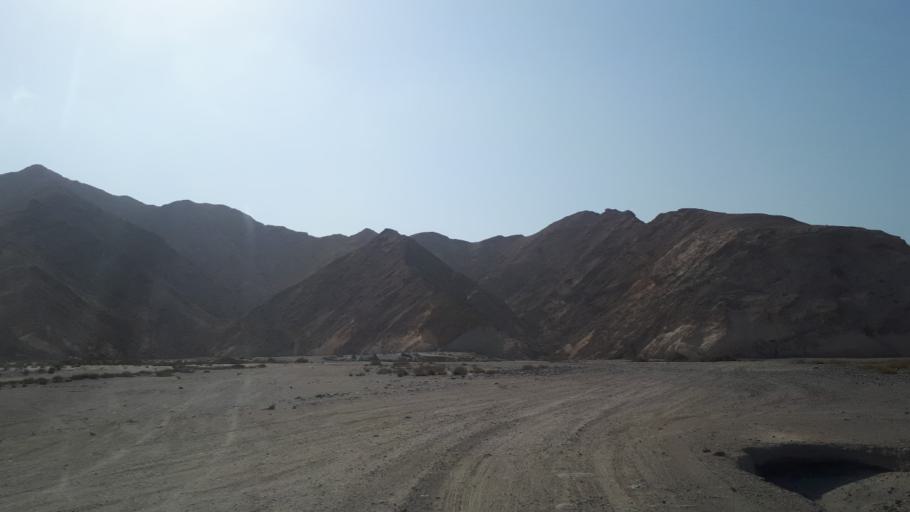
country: OM
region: Muhafazat Masqat
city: Muscat
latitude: 23.5437
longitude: 58.6680
